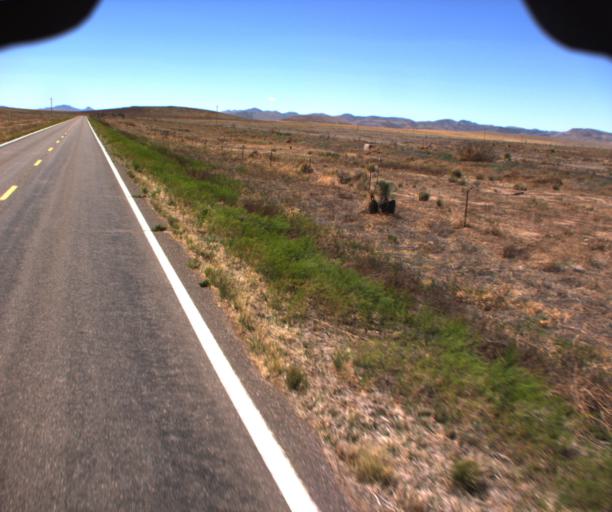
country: US
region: Arizona
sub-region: Cochise County
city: Douglas
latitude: 31.6259
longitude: -109.2060
